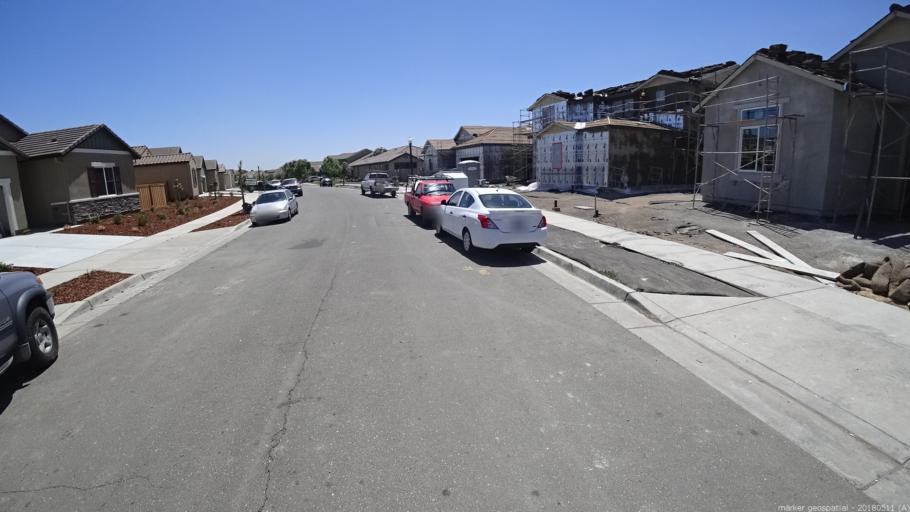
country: US
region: California
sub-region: Yolo County
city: West Sacramento
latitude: 38.6458
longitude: -121.5519
